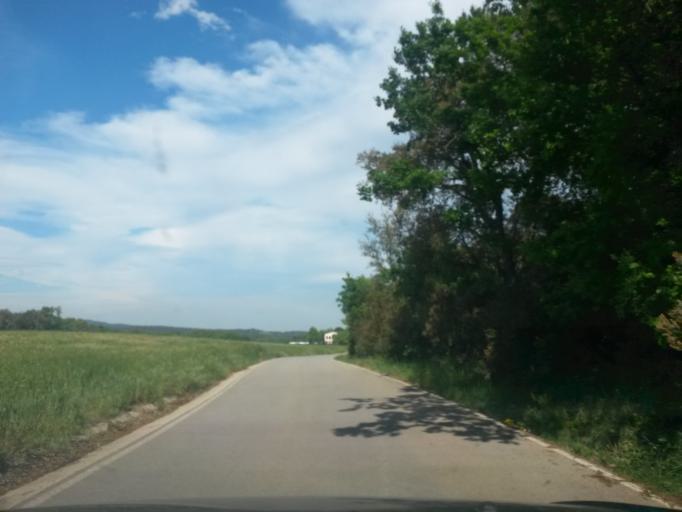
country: ES
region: Catalonia
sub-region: Provincia de Girona
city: Brunyola
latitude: 41.9101
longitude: 2.6995
